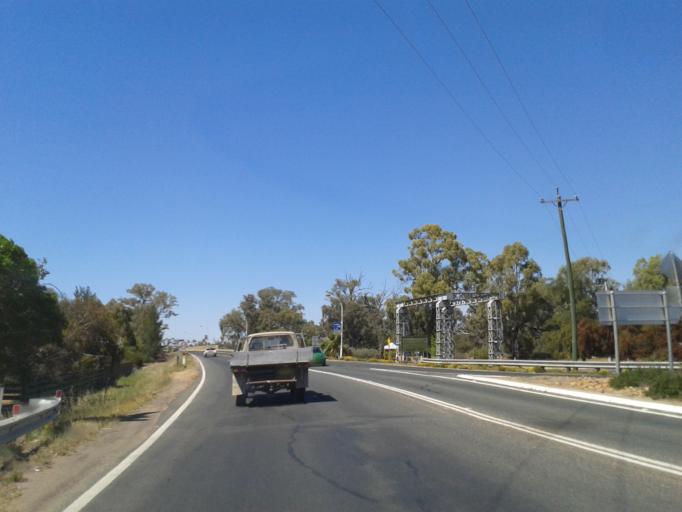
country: AU
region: New South Wales
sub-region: Wentworth
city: Dareton
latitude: -34.1064
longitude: 141.9234
